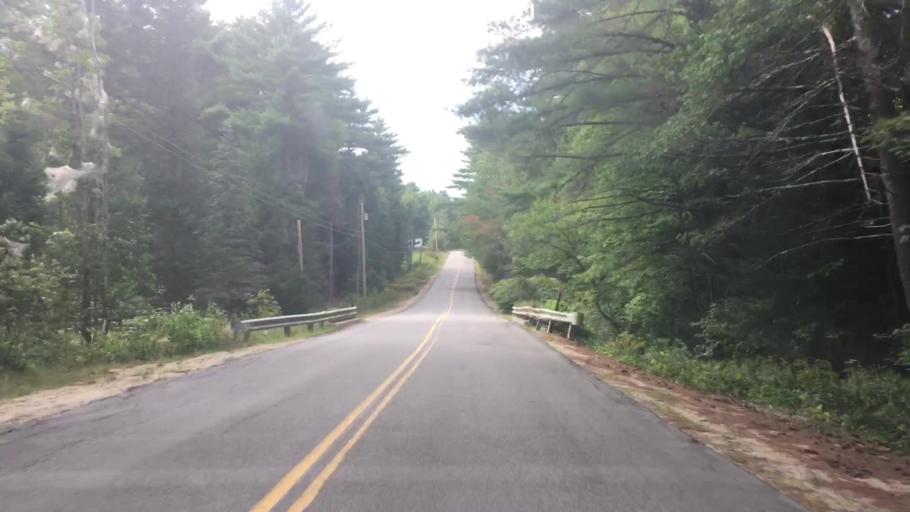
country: US
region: Maine
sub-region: Oxford County
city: Oxford
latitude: 44.0598
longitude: -70.5624
